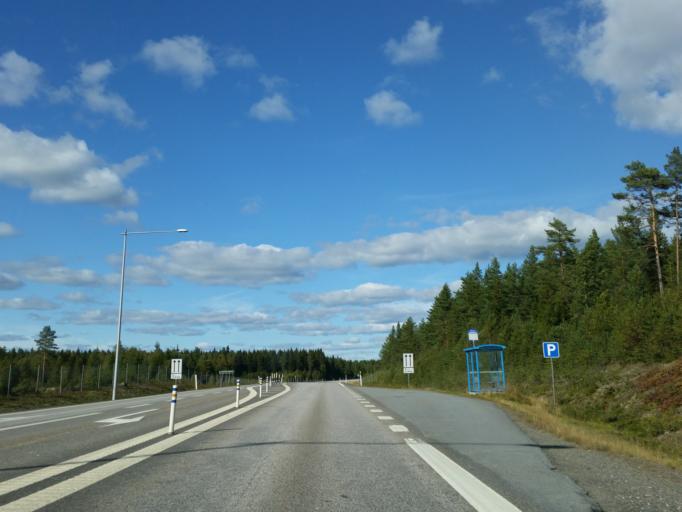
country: SE
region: Vaesterbotten
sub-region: Robertsfors Kommun
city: Robertsfors
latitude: 64.1180
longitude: 20.8816
